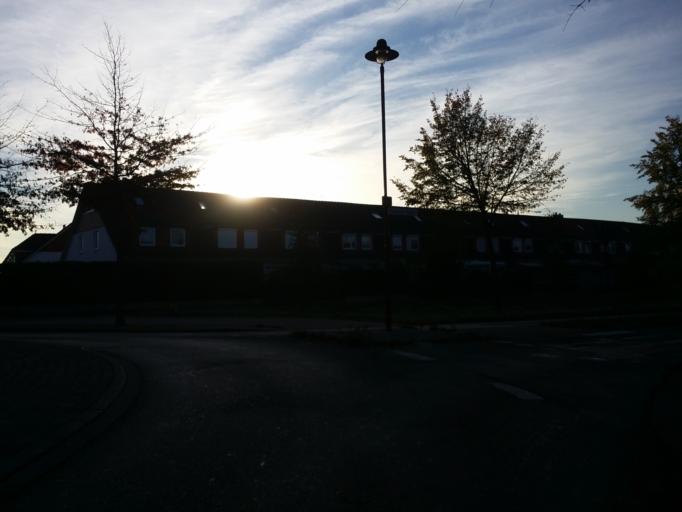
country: DE
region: Lower Saxony
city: Stuhr
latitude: 53.0020
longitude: 8.7763
